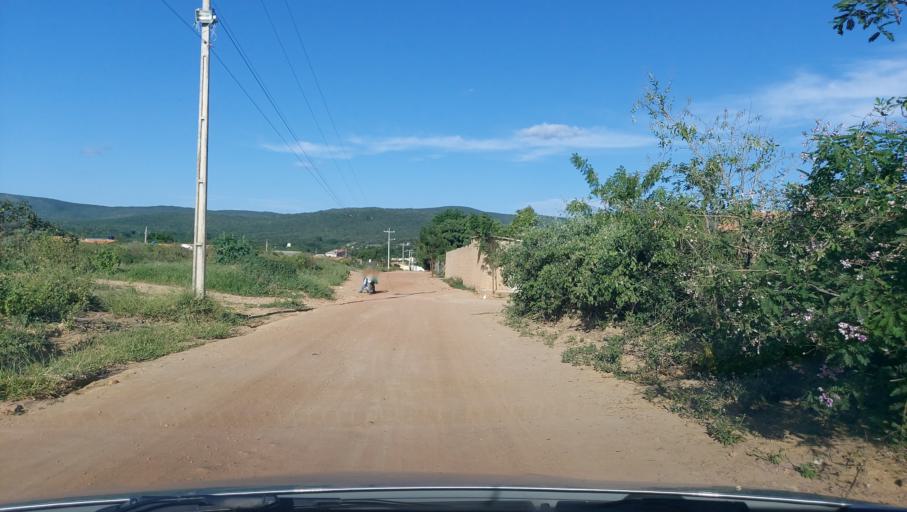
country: BR
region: Bahia
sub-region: Oliveira Dos Brejinhos
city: Beira Rio
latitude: -12.0037
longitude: -42.6316
